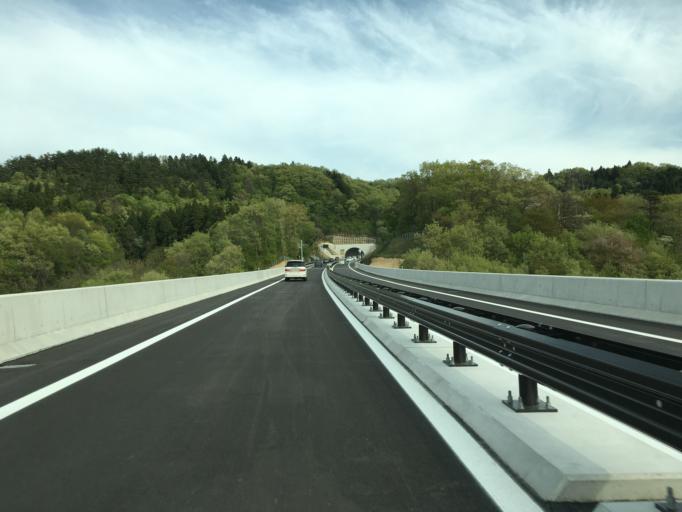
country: JP
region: Fukushima
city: Hobaramachi
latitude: 37.7884
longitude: 140.5607
